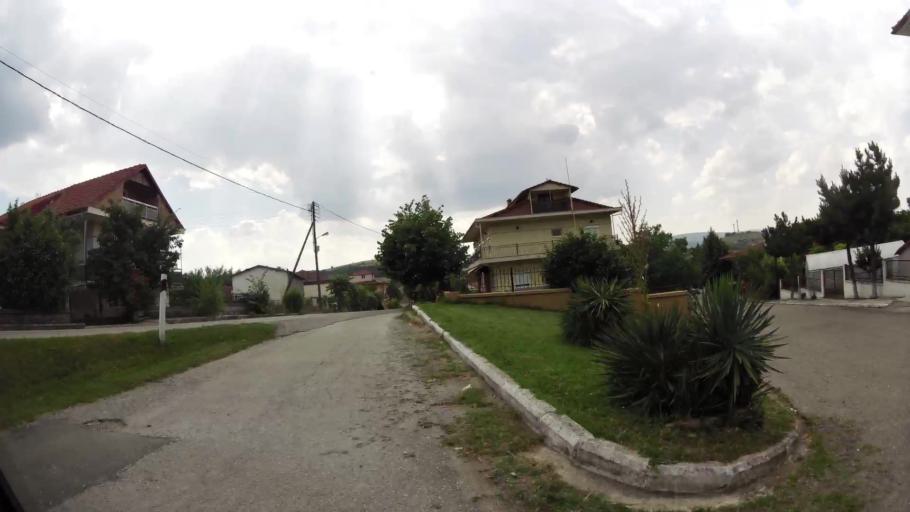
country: GR
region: West Macedonia
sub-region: Nomos Kozanis
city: Koila
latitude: 40.3498
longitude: 21.8307
